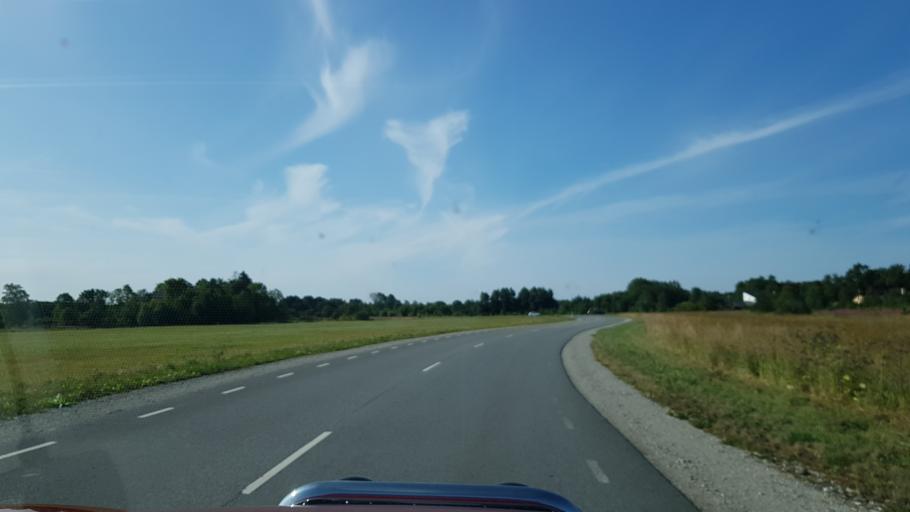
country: EE
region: Harju
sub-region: Rae vald
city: Jueri
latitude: 59.3749
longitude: 24.9258
